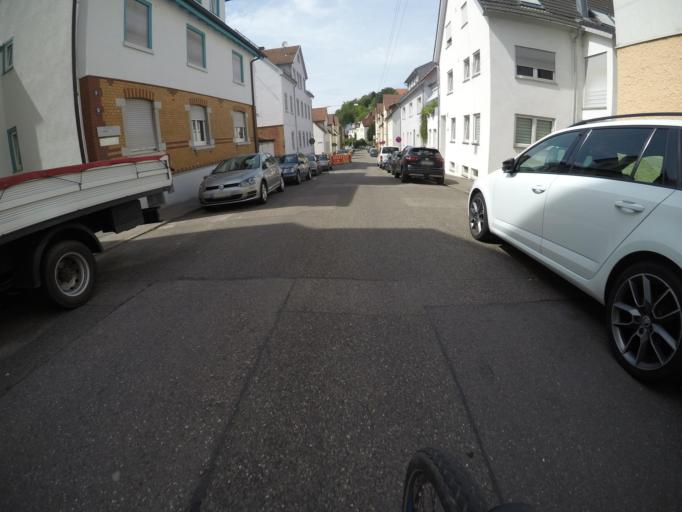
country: DE
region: Baden-Wuerttemberg
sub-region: Regierungsbezirk Stuttgart
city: Ostfildern
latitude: 48.7650
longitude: 9.2695
